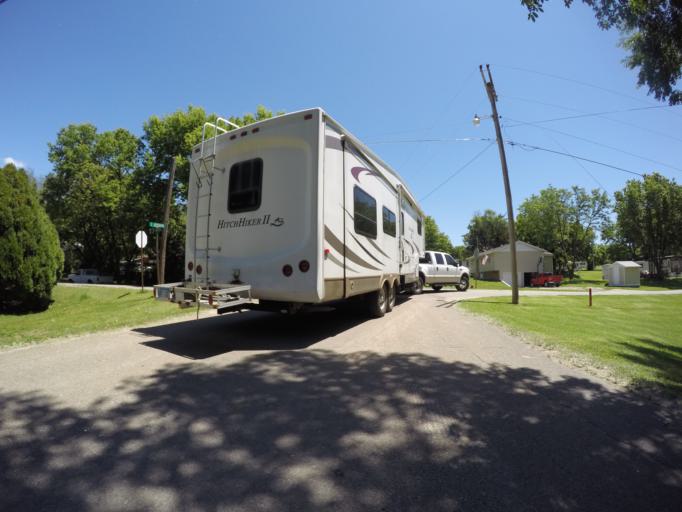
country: US
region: Kansas
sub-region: Jewell County
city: Mankato
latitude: 39.7868
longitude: -98.2048
